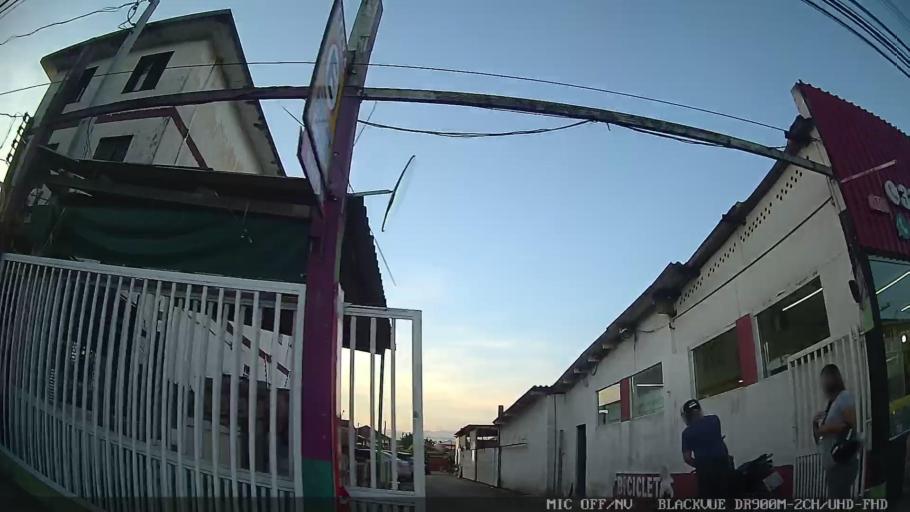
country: BR
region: Sao Paulo
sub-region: Guaruja
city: Guaruja
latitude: -23.9916
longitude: -46.2757
